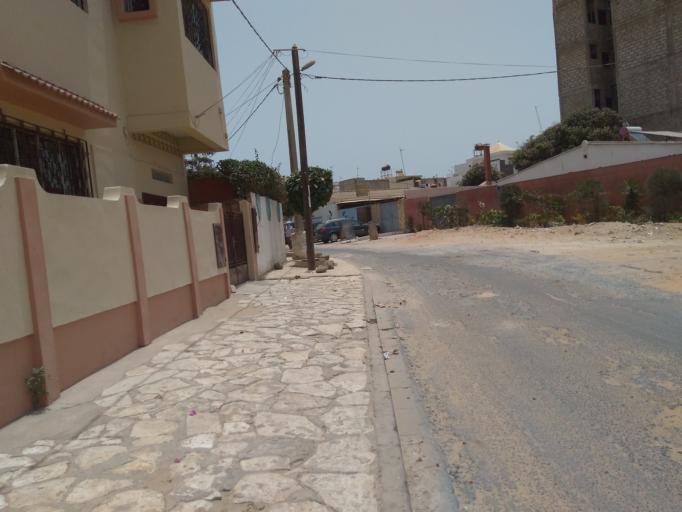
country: SN
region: Dakar
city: Grand Dakar
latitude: 14.7285
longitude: -17.4631
